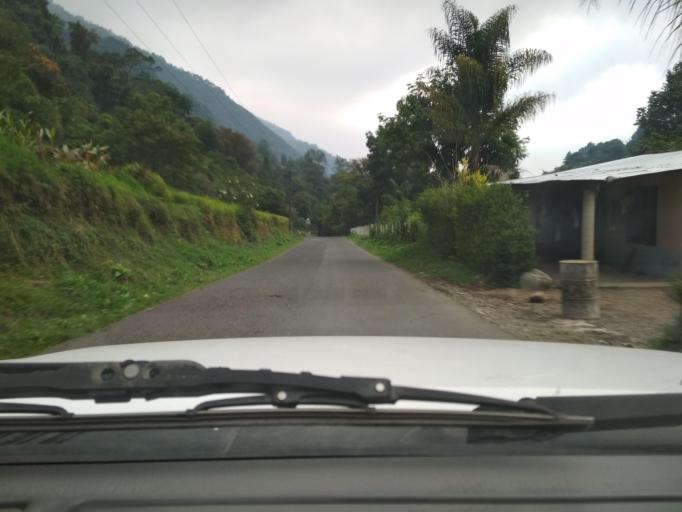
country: MX
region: Veracruz
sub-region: La Perla
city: Barrio de San Miguel
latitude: 18.9401
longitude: -97.1292
